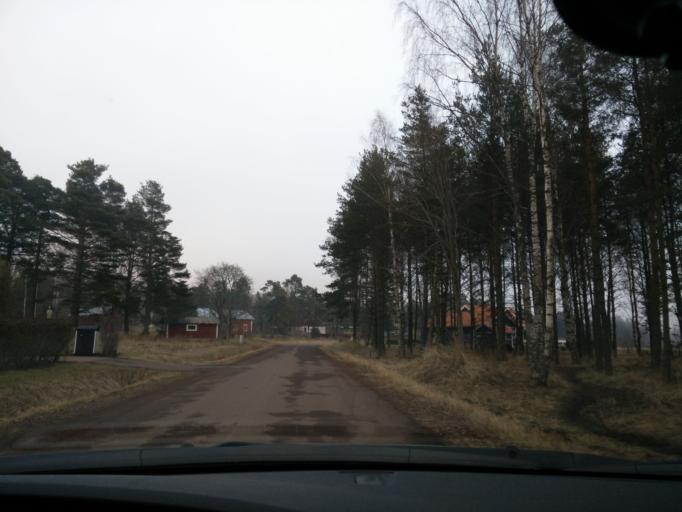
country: AX
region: Mariehamns stad
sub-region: Mariehamn
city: Mariehamn
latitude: 60.1303
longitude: 19.9170
